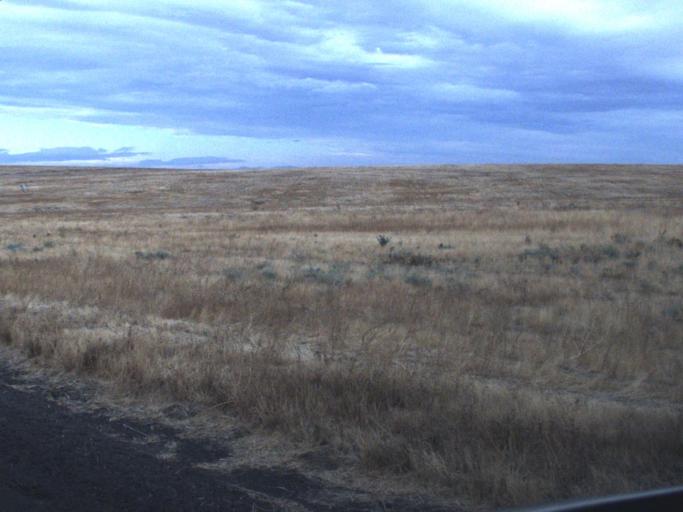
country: US
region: Washington
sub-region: Adams County
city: Ritzville
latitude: 47.4282
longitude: -118.7146
